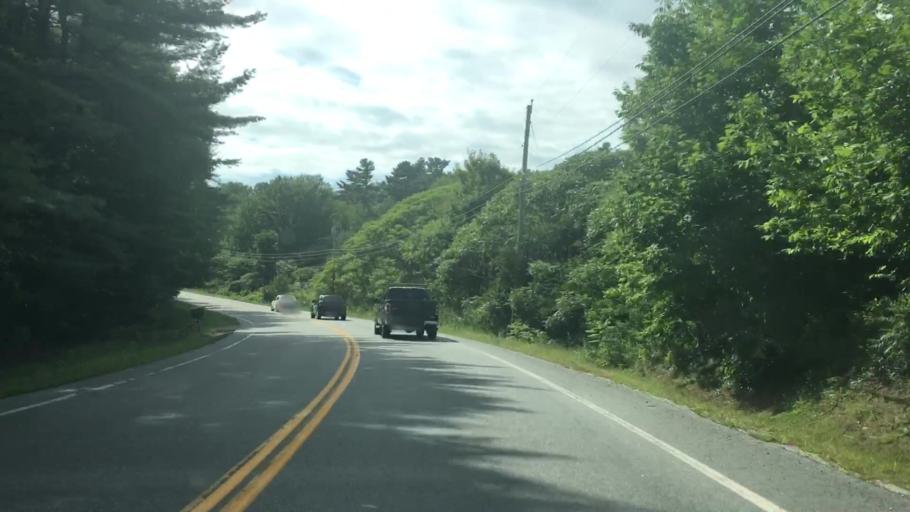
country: US
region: Maine
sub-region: Cumberland County
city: Raymond
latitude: 43.9866
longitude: -70.4869
